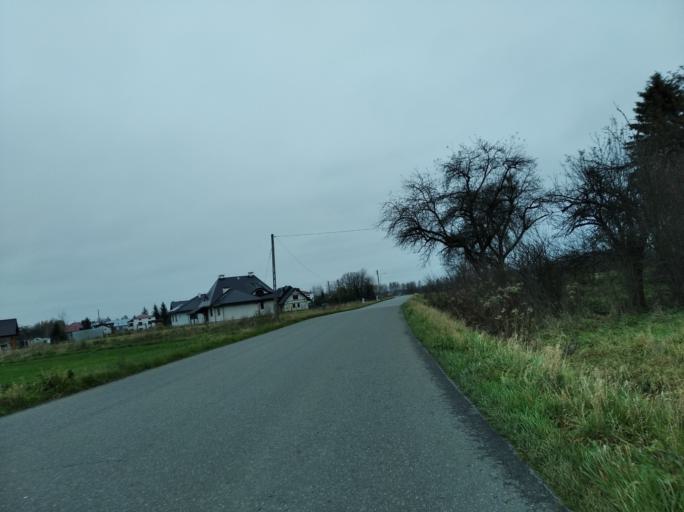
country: PL
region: Subcarpathian Voivodeship
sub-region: Powiat krosnienski
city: Chorkowka
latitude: 49.6802
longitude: 21.6772
